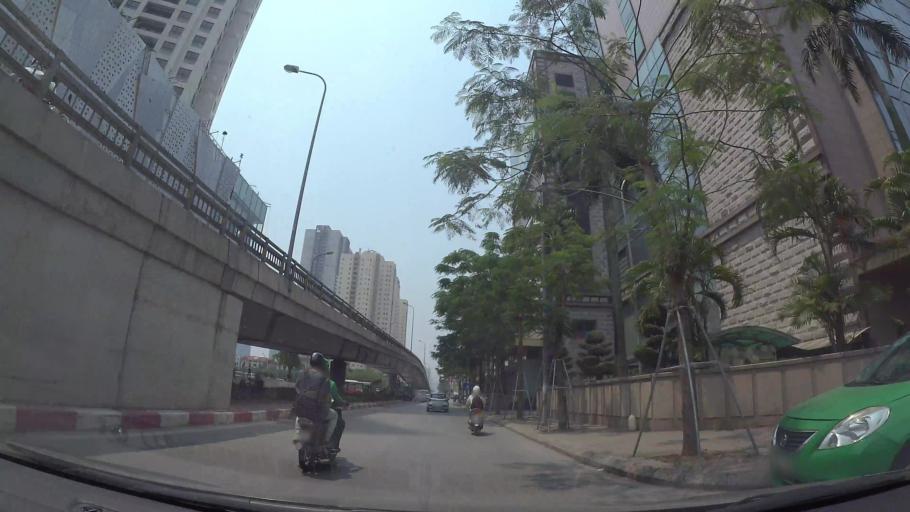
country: VN
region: Ha Noi
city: Thanh Xuan
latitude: 21.0070
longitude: 105.7965
